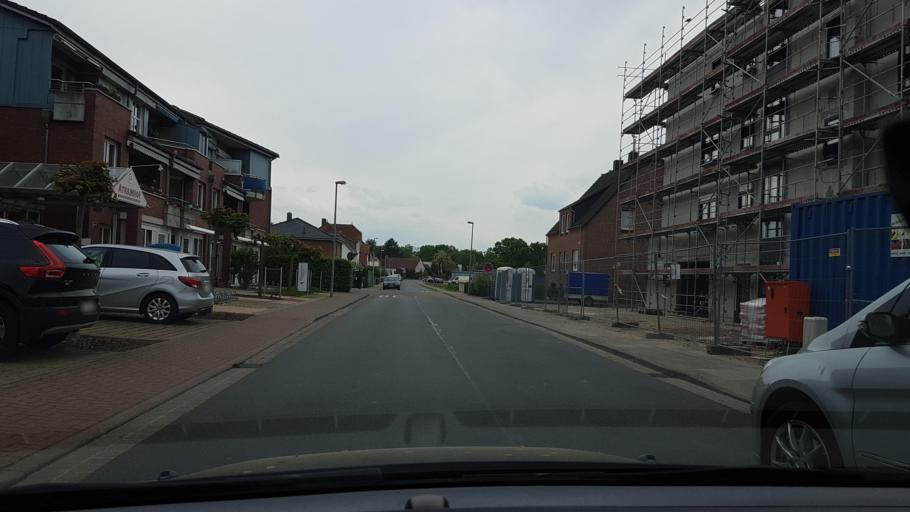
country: DE
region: Lower Saxony
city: Garbsen-Mitte
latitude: 52.4351
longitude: 9.6071
